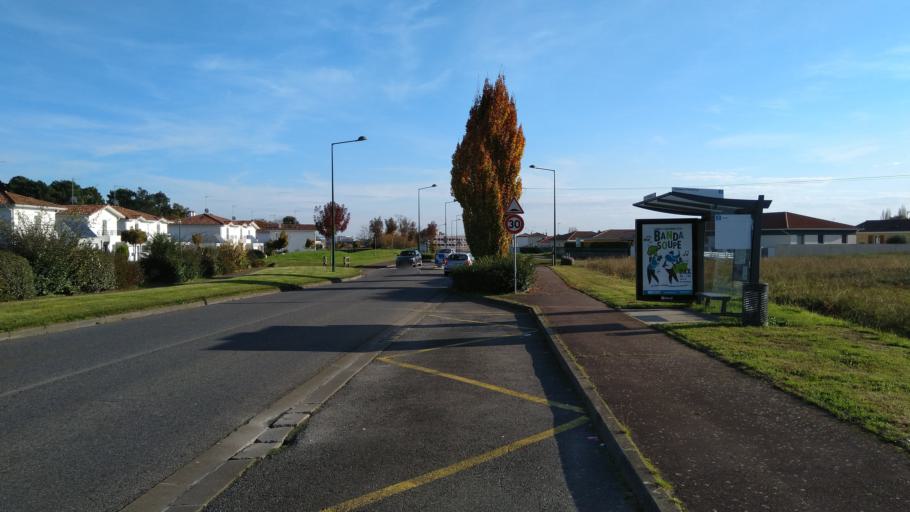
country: FR
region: Aquitaine
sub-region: Departement des Landes
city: Saint-Paul-les-Dax
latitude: 43.7351
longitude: -1.0479
